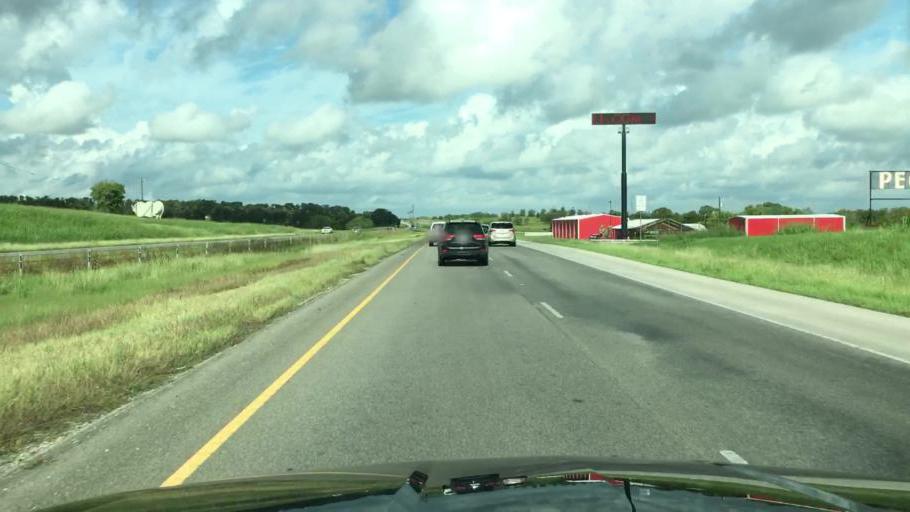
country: US
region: Texas
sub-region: Bastrop County
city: Wyldwood
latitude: 30.1652
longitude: -97.5094
